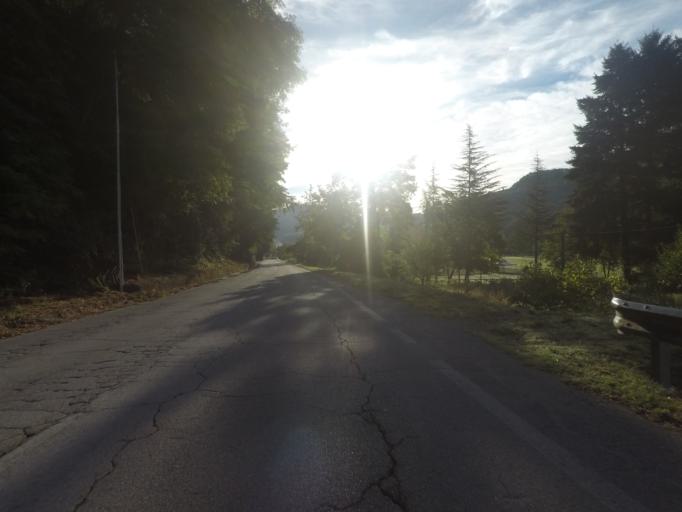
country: IT
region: Tuscany
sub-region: Provincia di Lucca
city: Pescaglia
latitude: 43.9524
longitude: 10.4385
